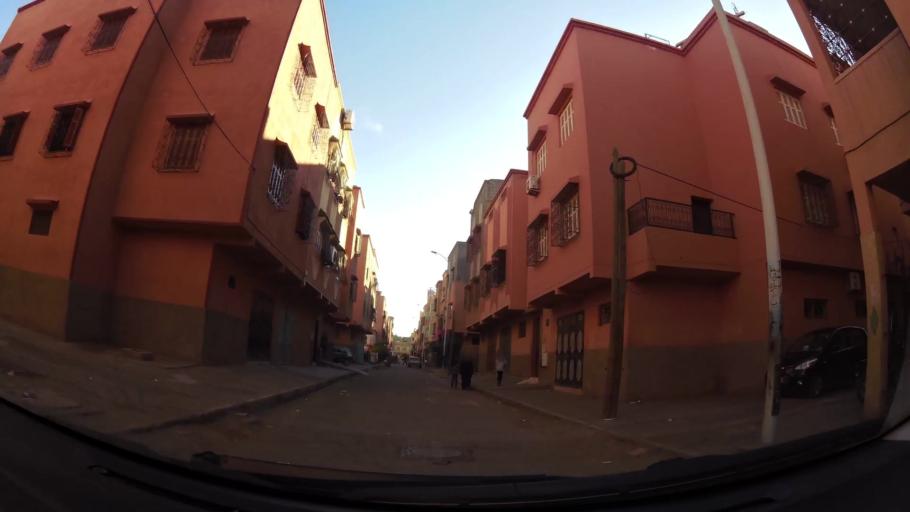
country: MA
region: Marrakech-Tensift-Al Haouz
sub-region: Marrakech
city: Marrakesh
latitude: 31.6189
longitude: -8.0655
